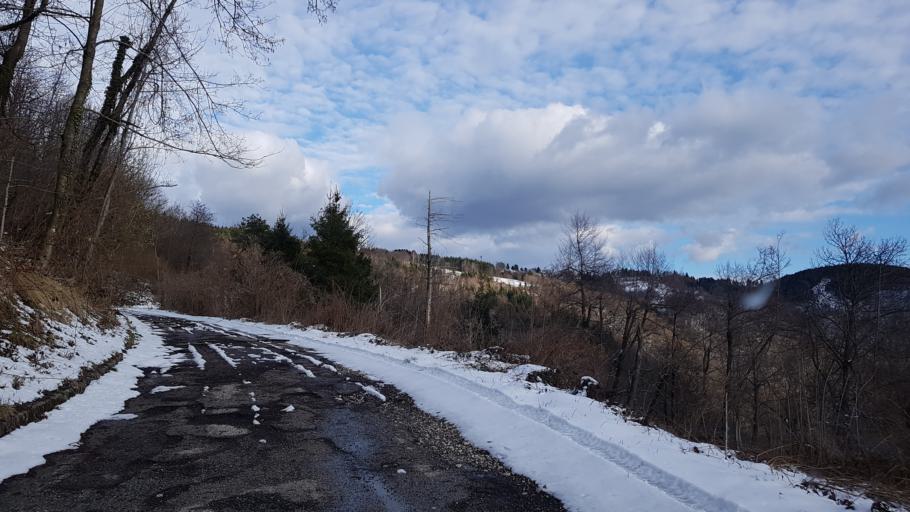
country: IT
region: Friuli Venezia Giulia
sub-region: Provincia di Udine
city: Torreano
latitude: 46.1791
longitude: 13.3982
